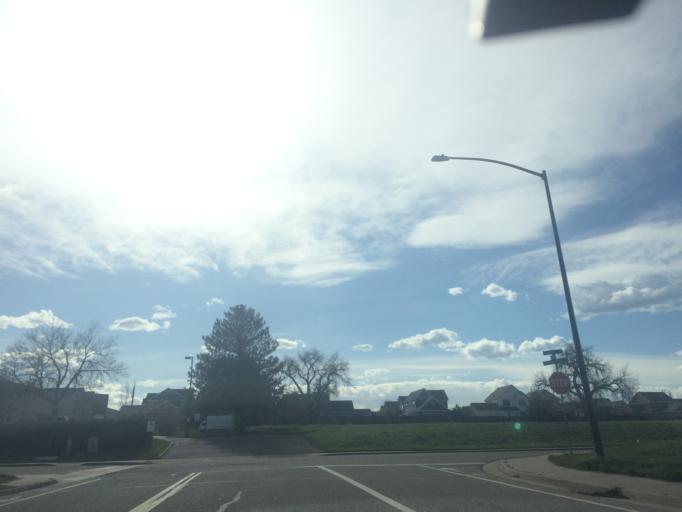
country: US
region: Colorado
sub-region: Boulder County
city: Lafayette
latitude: 40.0039
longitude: -105.1059
